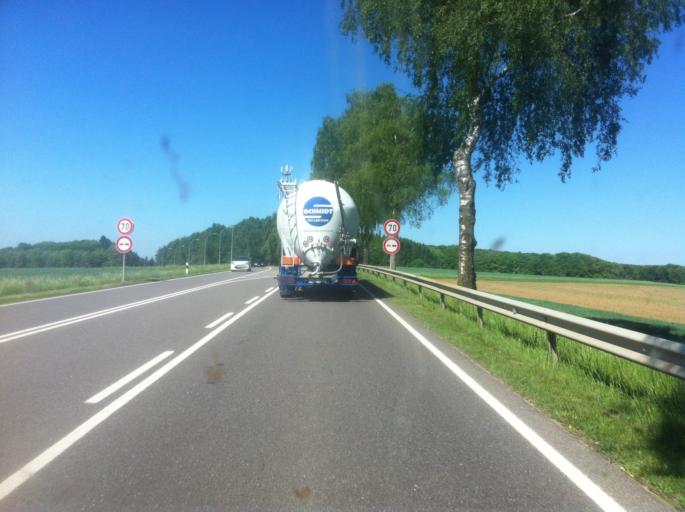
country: LU
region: Grevenmacher
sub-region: Canton d'Echternach
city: Consdorf
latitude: 49.7478
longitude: 6.3142
